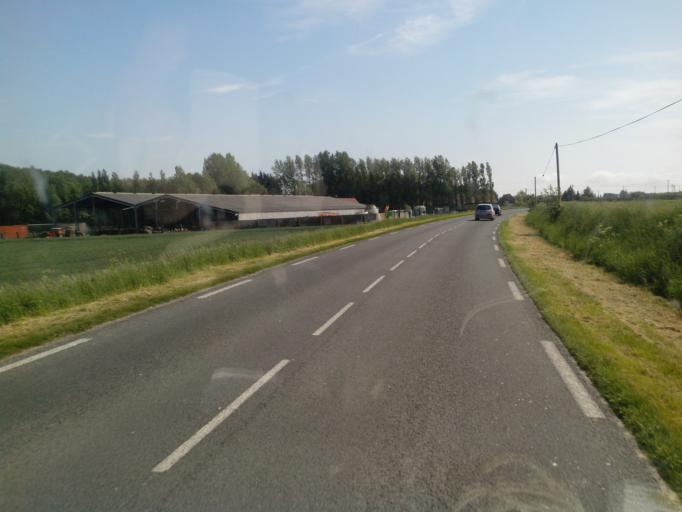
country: FR
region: Picardie
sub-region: Departement de la Somme
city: Quend
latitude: 50.3322
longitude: 1.6438
